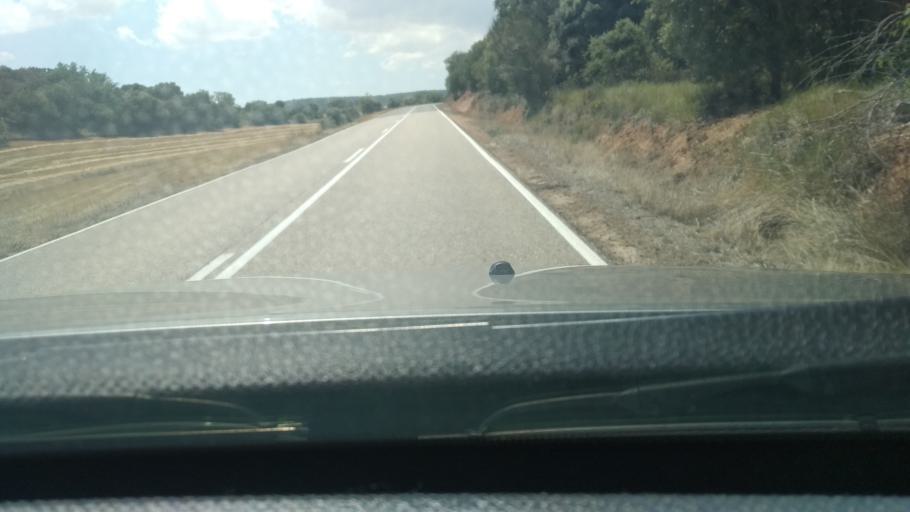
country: ES
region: Castille and Leon
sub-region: Provincia de Burgos
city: Quintanilla de la Mata
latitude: 41.9861
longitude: -3.7798
